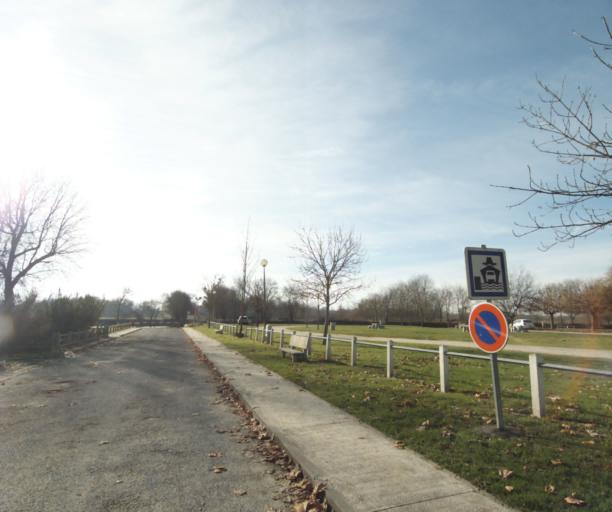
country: FR
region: Poitou-Charentes
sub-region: Departement de la Charente-Maritime
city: Chaniers
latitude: 45.7154
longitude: -0.5594
